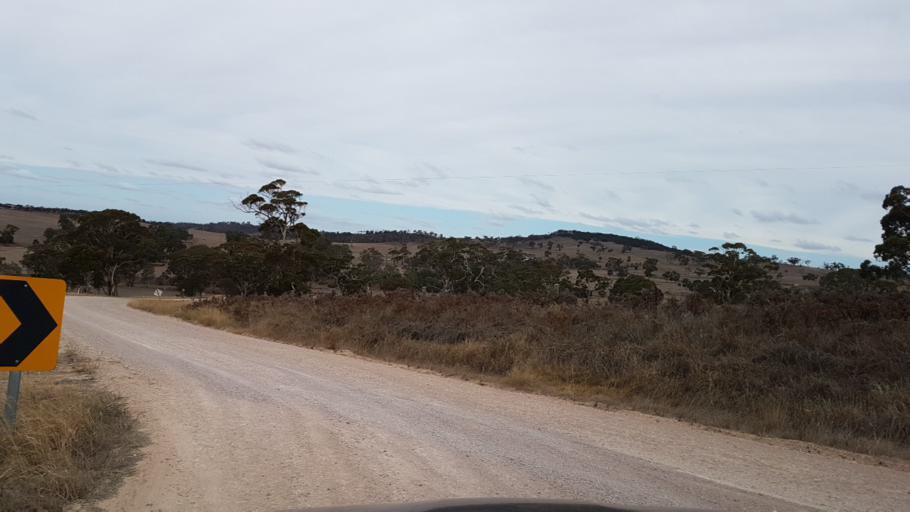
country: AU
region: South Australia
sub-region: Adelaide Hills
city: Birdwood
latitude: -34.9177
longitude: 139.0704
